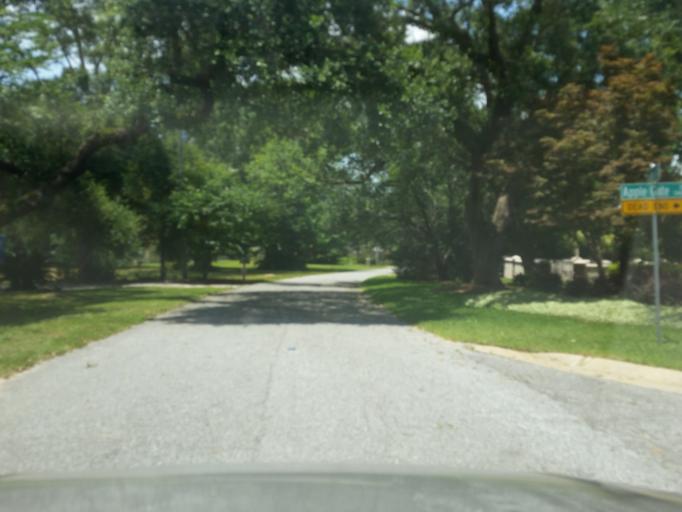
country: US
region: Florida
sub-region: Escambia County
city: Ferry Pass
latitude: 30.5351
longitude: -87.1952
